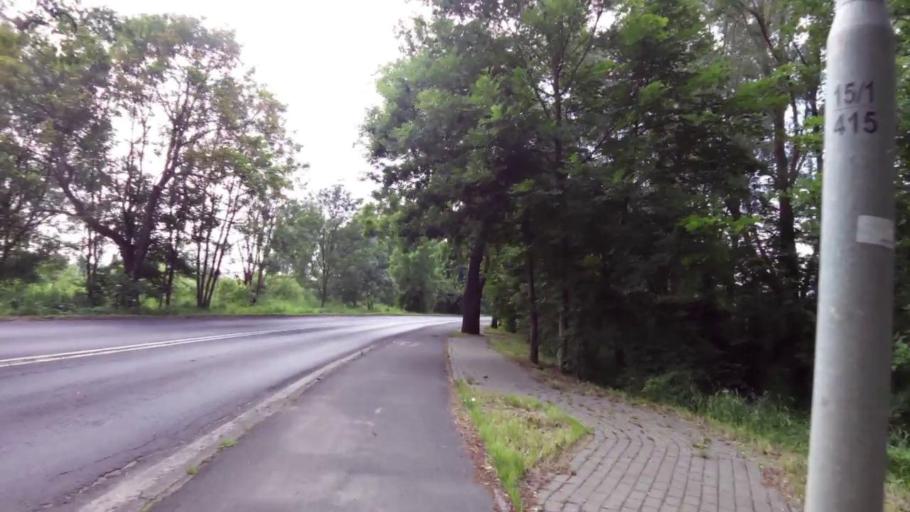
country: PL
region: West Pomeranian Voivodeship
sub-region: Szczecin
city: Szczecin
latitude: 53.3952
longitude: 14.6553
